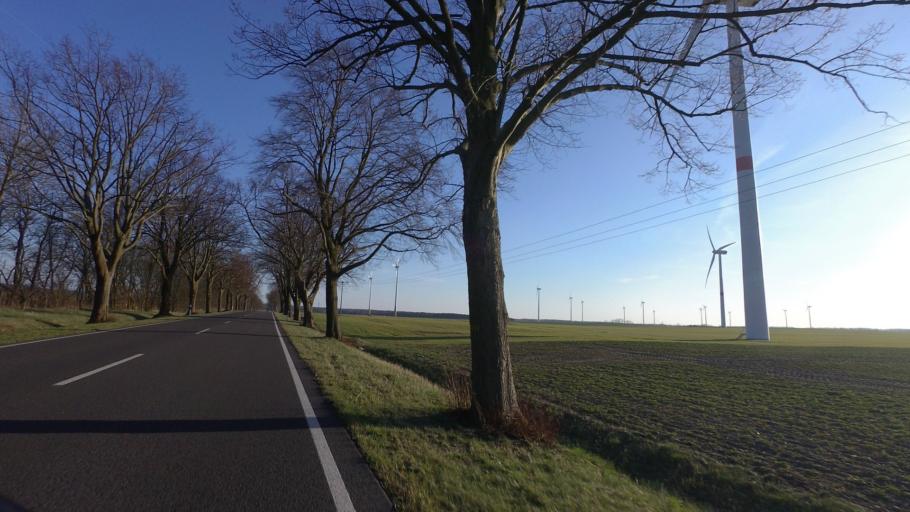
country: DE
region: Brandenburg
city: Werftpfuhl
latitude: 52.6985
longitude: 13.8364
